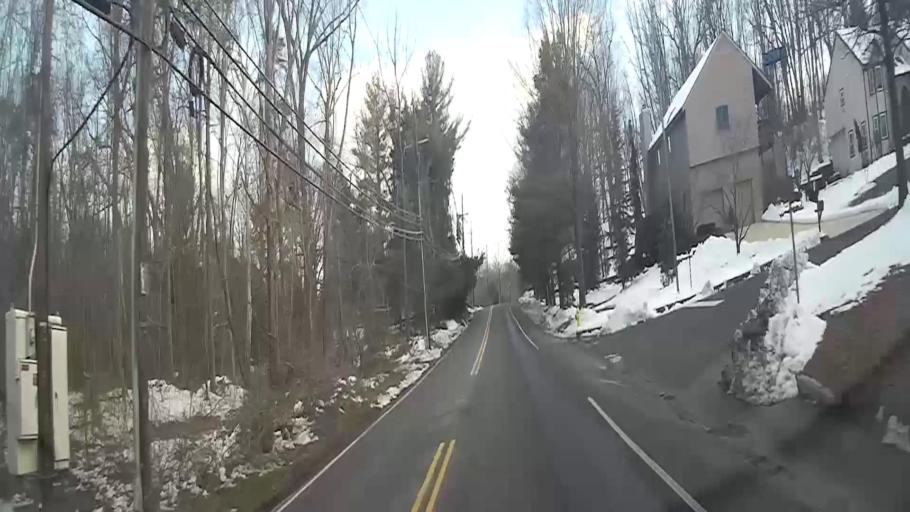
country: US
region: New Jersey
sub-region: Camden County
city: Gibbsboro
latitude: 39.8631
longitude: -74.9542
